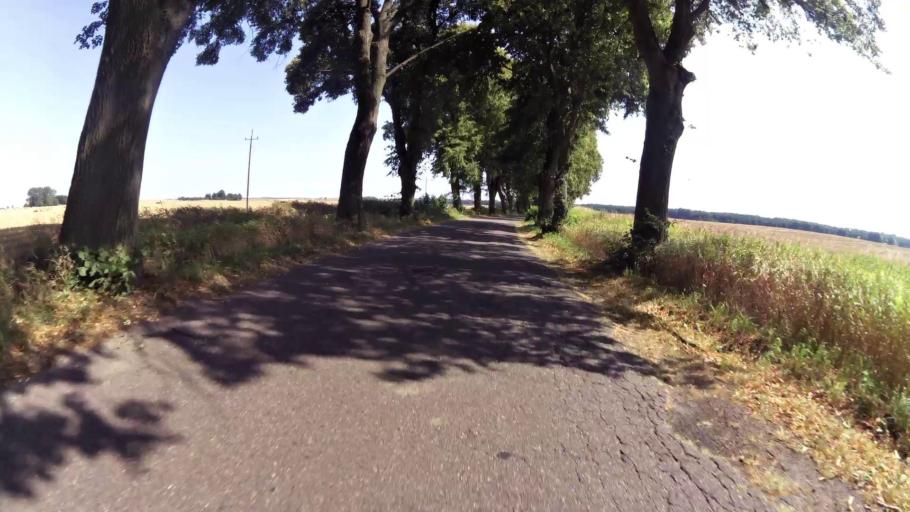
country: PL
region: West Pomeranian Voivodeship
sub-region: Powiat walecki
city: Walcz
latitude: 53.2003
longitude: 16.5107
